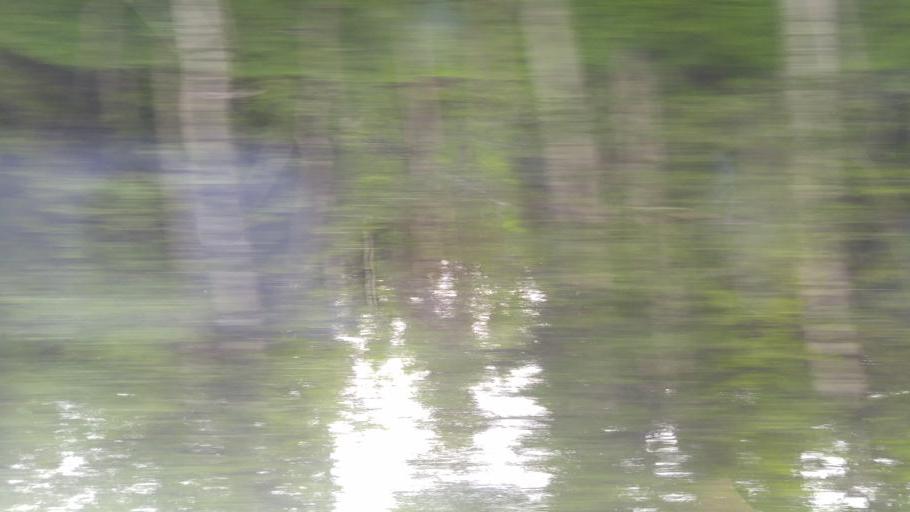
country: NO
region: Nord-Trondelag
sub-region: Meraker
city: Meraker
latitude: 63.3127
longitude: 12.2457
